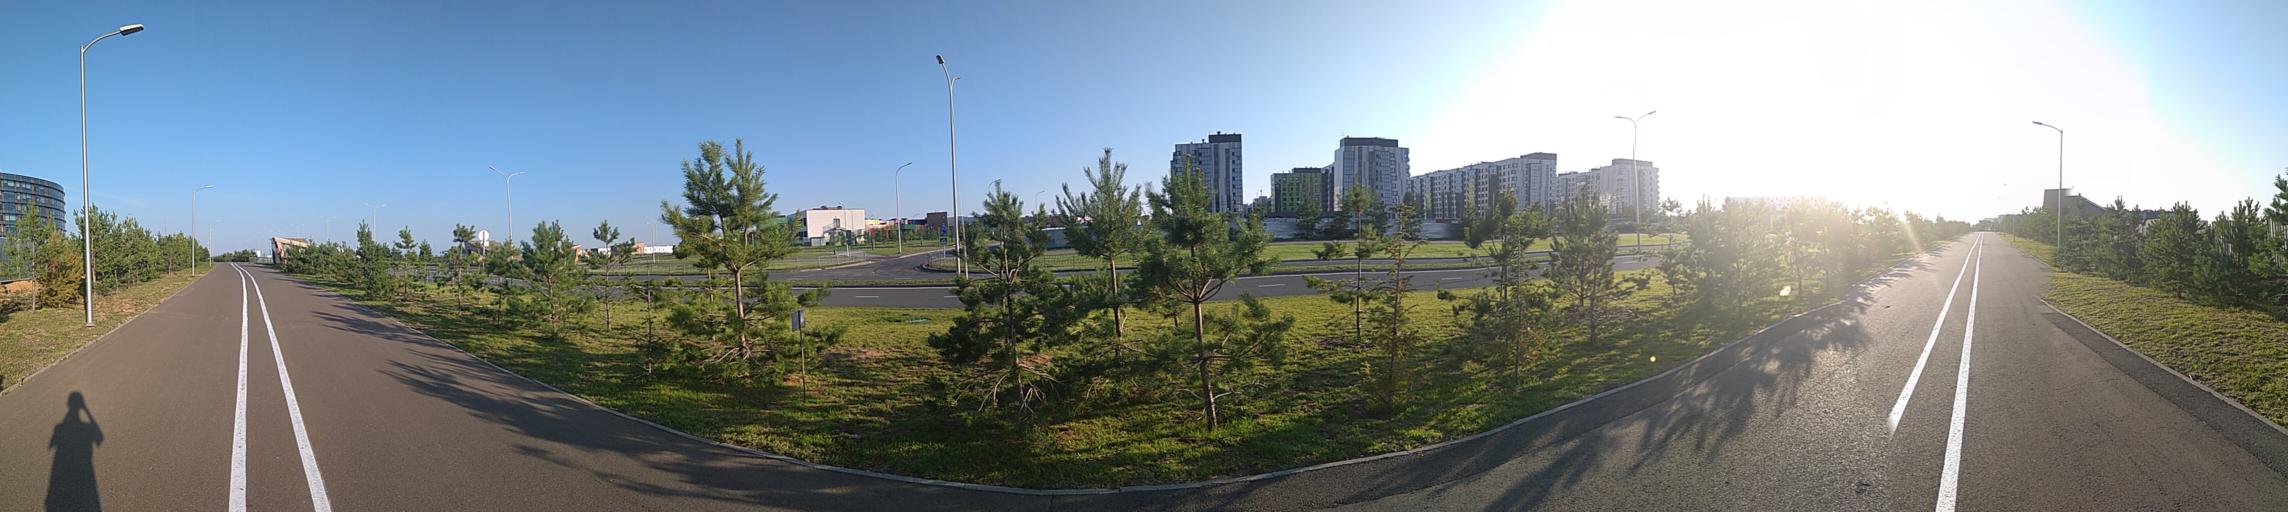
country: RU
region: Tatarstan
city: Sviyazhsk
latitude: 55.7513
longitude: 48.7477
